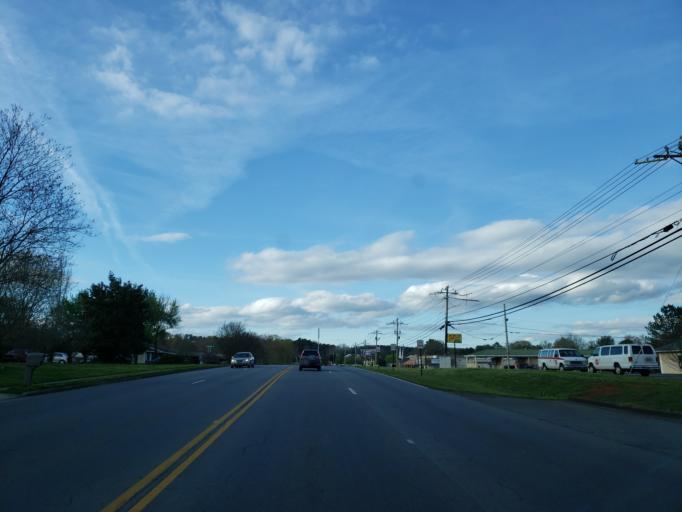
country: US
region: Georgia
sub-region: Bartow County
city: Cartersville
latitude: 34.2190
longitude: -84.8189
